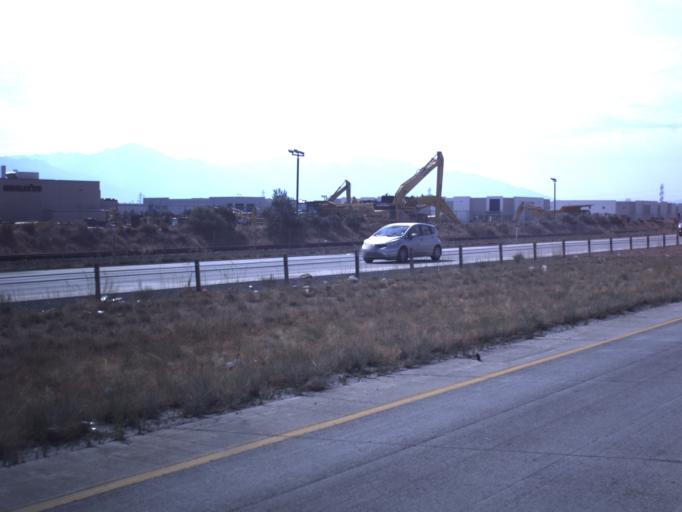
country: US
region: Utah
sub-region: Salt Lake County
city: West Valley City
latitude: 40.7393
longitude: -111.9903
